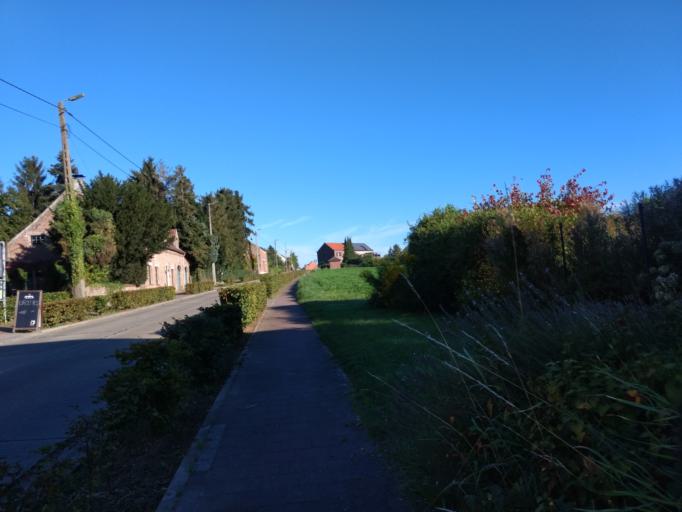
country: BE
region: Flanders
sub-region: Provincie Vlaams-Brabant
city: Bierbeek
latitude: 50.8387
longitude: 4.7333
